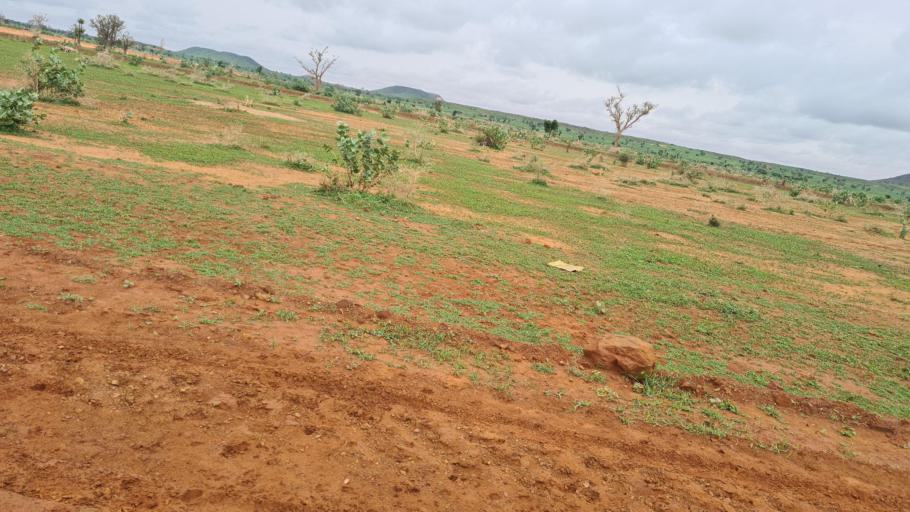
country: NE
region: Tahoua
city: Birni N Konni
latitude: 13.8117
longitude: 5.2429
